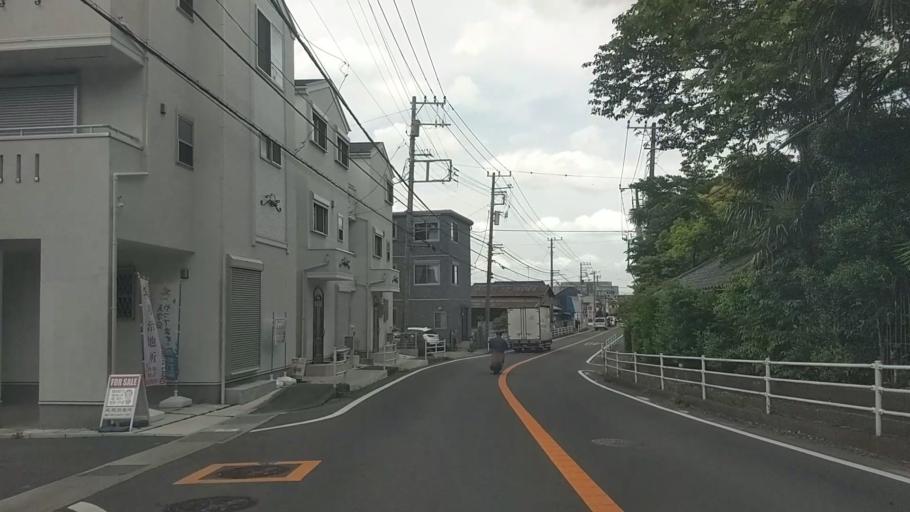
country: JP
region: Kanagawa
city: Fujisawa
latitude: 35.3260
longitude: 139.5084
